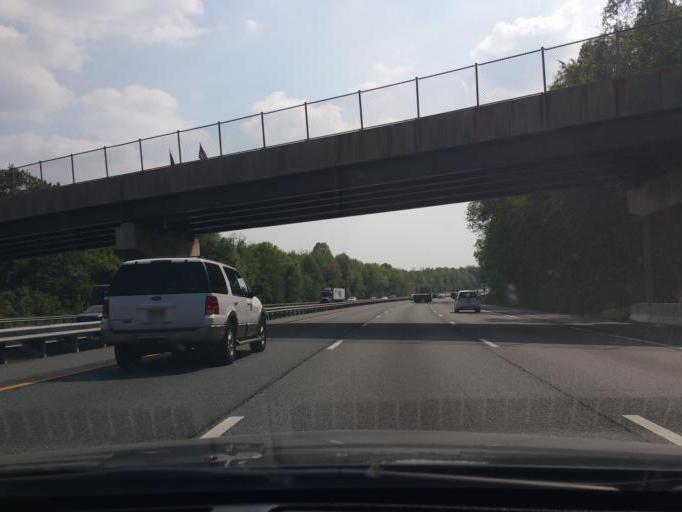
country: US
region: Maryland
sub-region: Harford County
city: Aberdeen
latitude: 39.5347
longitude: -76.1762
